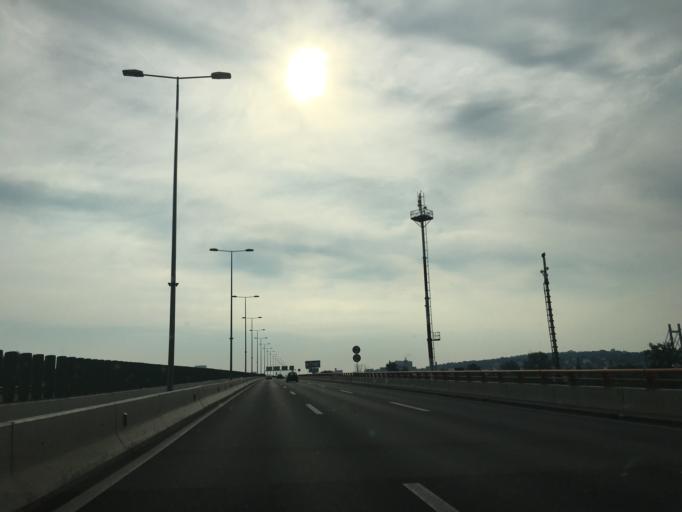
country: RS
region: Central Serbia
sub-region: Belgrade
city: Novi Beograd
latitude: 44.8063
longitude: 20.4334
